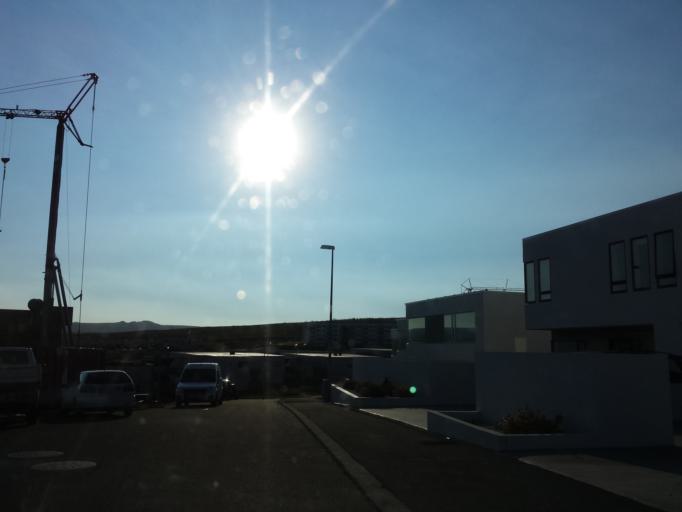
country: IS
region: Capital Region
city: Reykjavik
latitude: 64.0836
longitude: -21.8168
